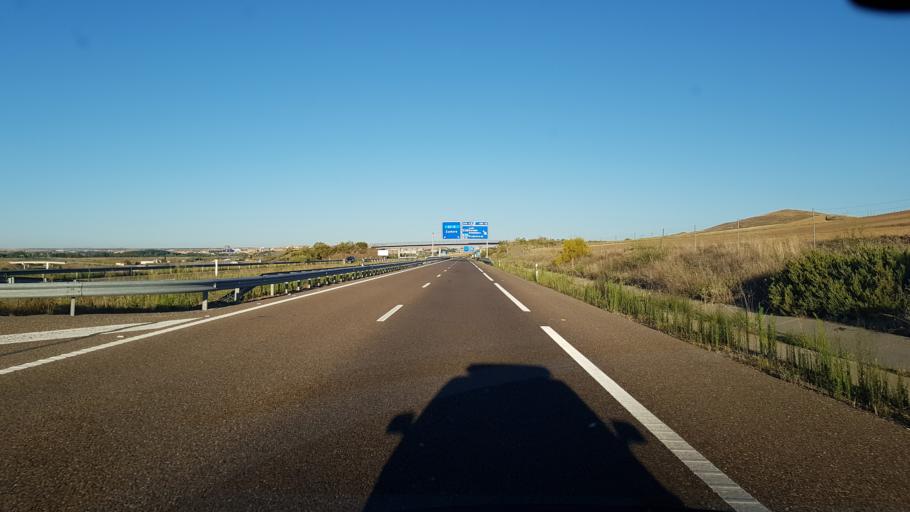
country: ES
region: Castille and Leon
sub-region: Provincia de Zamora
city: Monfarracinos
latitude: 41.5350
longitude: -5.6859
